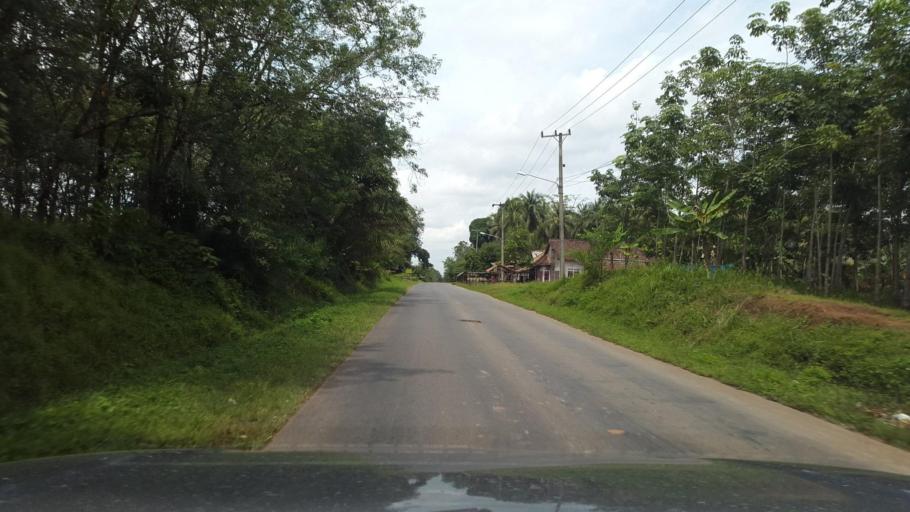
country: ID
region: South Sumatra
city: Gunungmegang Dalam
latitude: -3.3628
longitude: 103.9364
